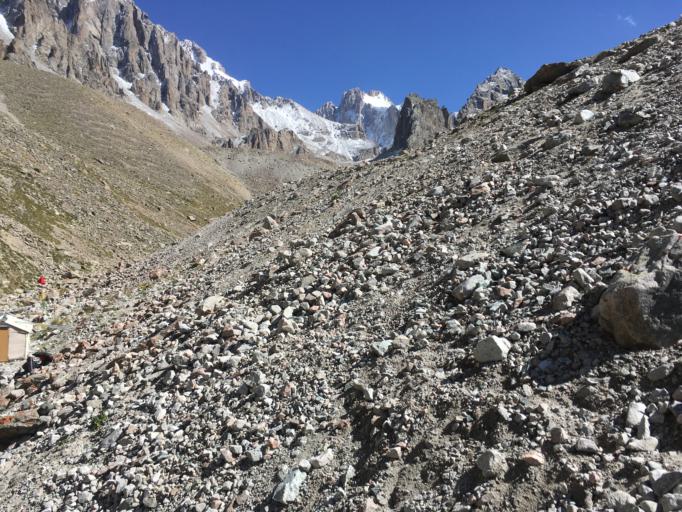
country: KG
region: Chuy
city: Bishkek
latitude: 42.5349
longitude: 74.5287
